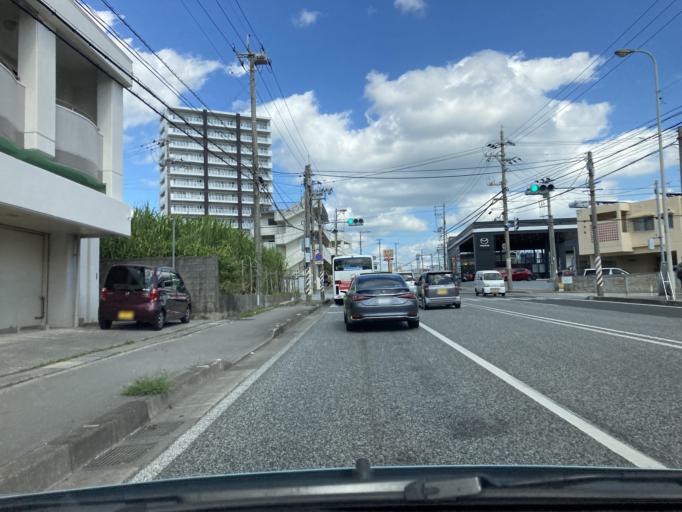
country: JP
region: Okinawa
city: Okinawa
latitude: 26.3648
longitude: 127.8147
